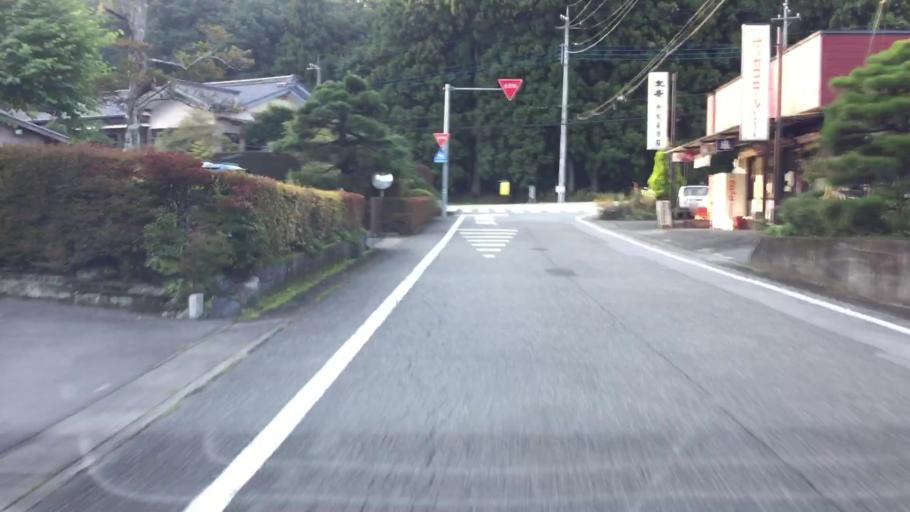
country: JP
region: Tochigi
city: Imaichi
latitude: 36.7655
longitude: 139.6790
